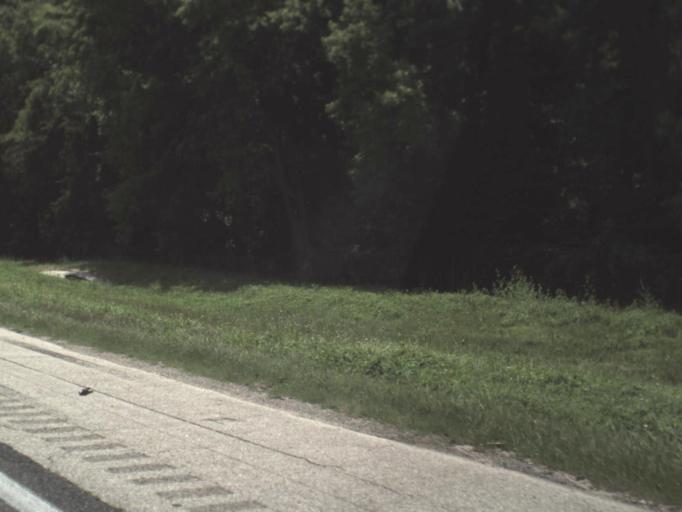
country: US
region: Florida
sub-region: Alachua County
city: Alachua
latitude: 29.6732
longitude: -82.4316
